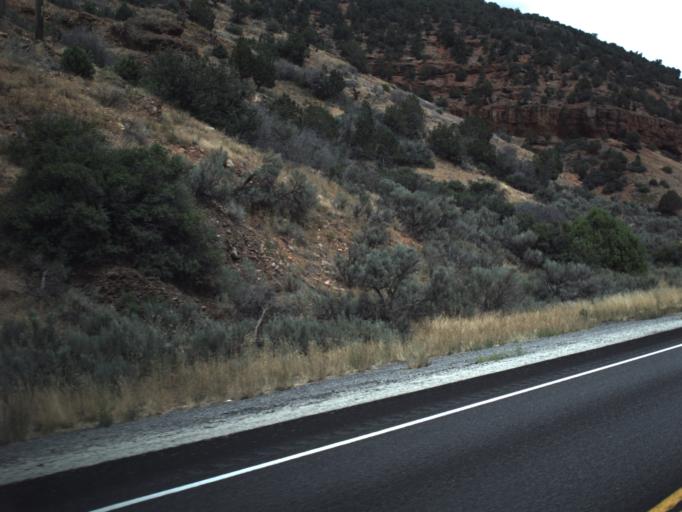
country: US
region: Utah
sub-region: Utah County
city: Mapleton
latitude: 39.9913
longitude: -111.3838
